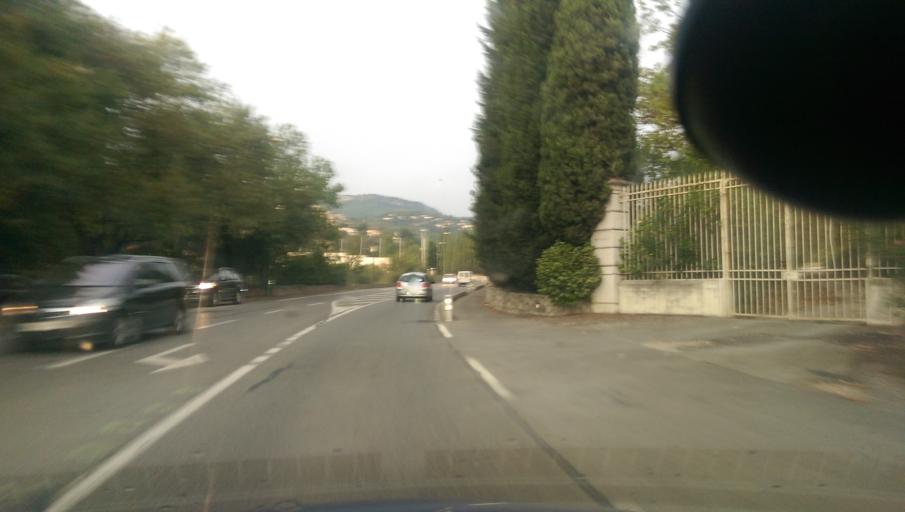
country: FR
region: Provence-Alpes-Cote d'Azur
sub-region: Departement des Alpes-Maritimes
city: Chateauneuf-Grasse
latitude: 43.6633
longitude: 6.9867
